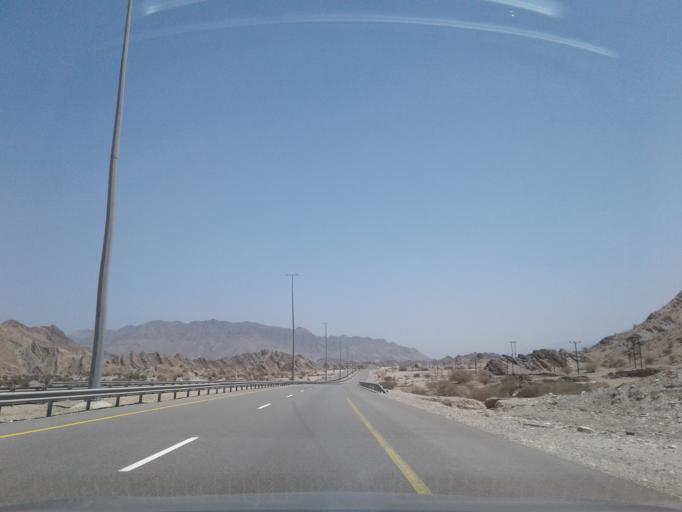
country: OM
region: Muhafazat Masqat
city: Muscat
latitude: 23.3502
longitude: 58.6893
